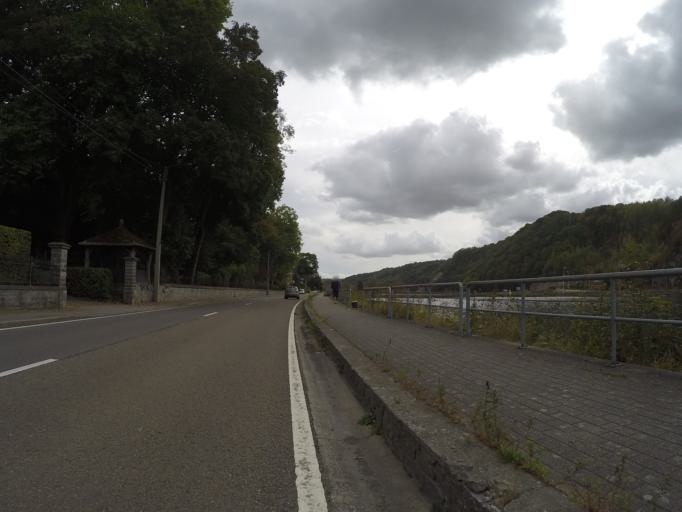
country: BE
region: Wallonia
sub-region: Province de Namur
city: Yvoir
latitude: 50.3352
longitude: 4.8738
